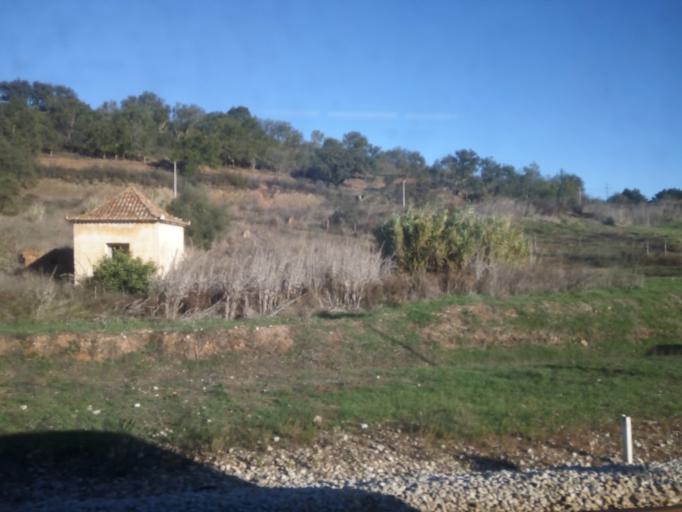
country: PT
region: Beja
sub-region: Odemira
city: Odemira
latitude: 37.4958
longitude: -8.4814
